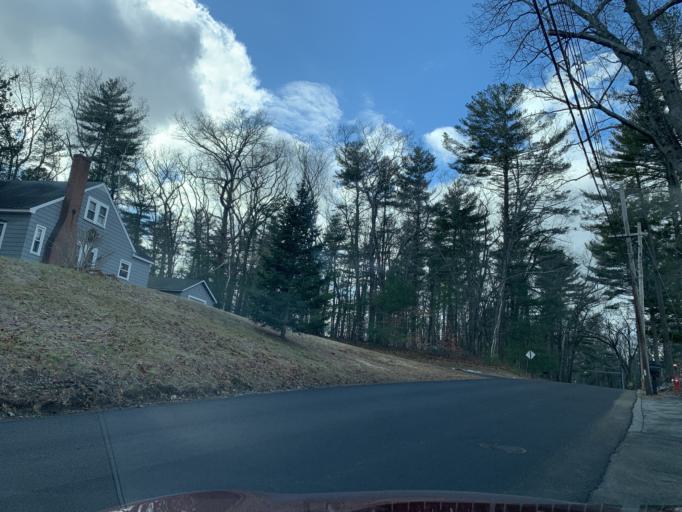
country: US
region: Massachusetts
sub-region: Essex County
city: Amesbury
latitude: 42.8346
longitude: -70.9325
